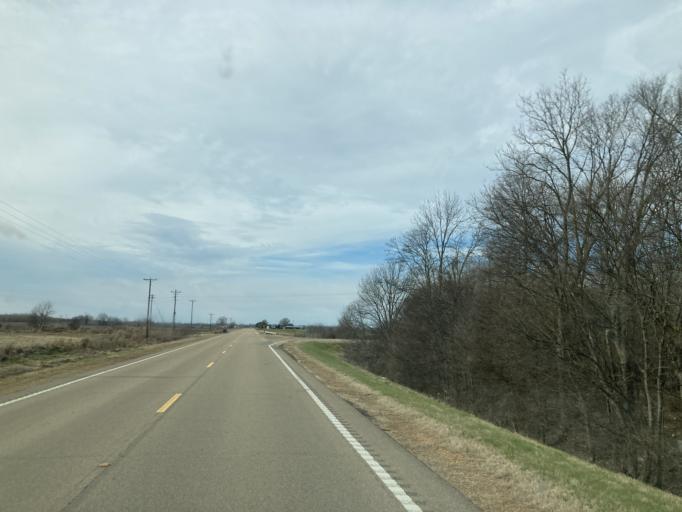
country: US
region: Mississippi
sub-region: Humphreys County
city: Belzoni
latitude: 33.1826
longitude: -90.6313
